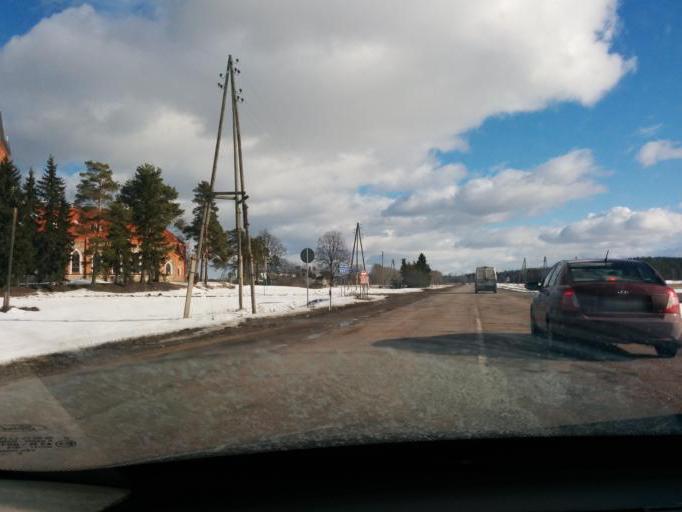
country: LV
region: Cesvaine
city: Cesvaine
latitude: 57.2389
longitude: 26.4022
